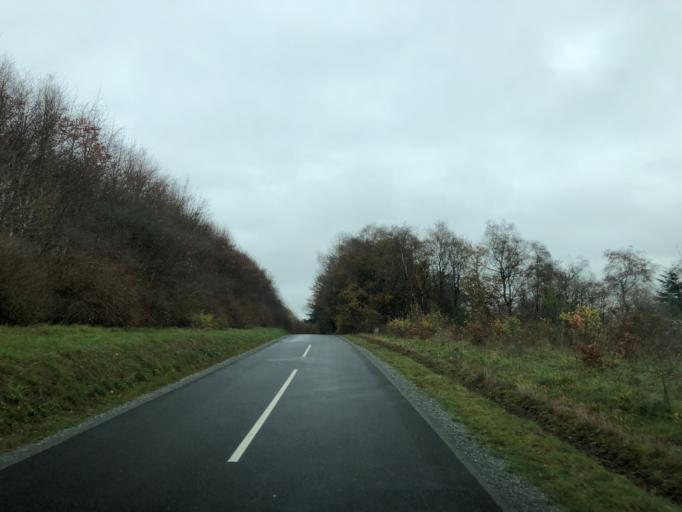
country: DK
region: Central Jutland
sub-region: Silkeborg Kommune
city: Virklund
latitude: 56.0676
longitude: 9.4905
